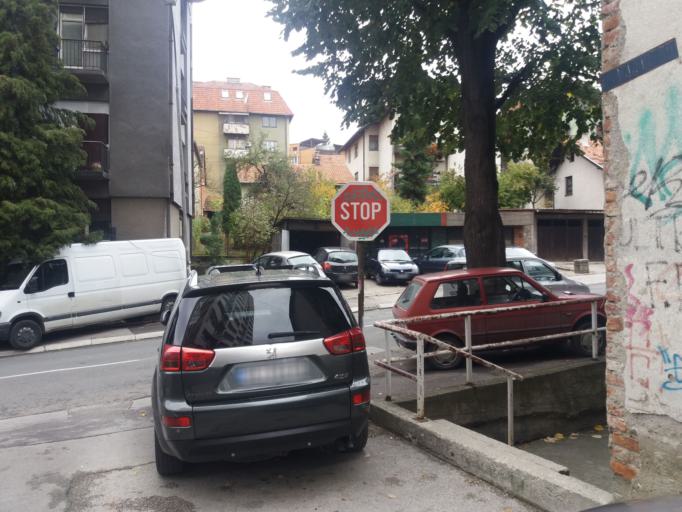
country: RS
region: Central Serbia
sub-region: Zlatiborski Okrug
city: Uzice
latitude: 43.8595
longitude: 19.8398
